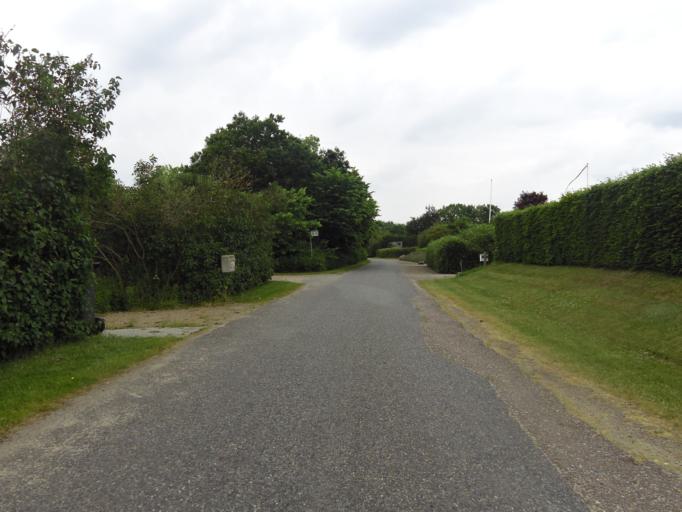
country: DK
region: South Denmark
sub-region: Esbjerg Kommune
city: Ribe
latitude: 55.3163
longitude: 8.8539
